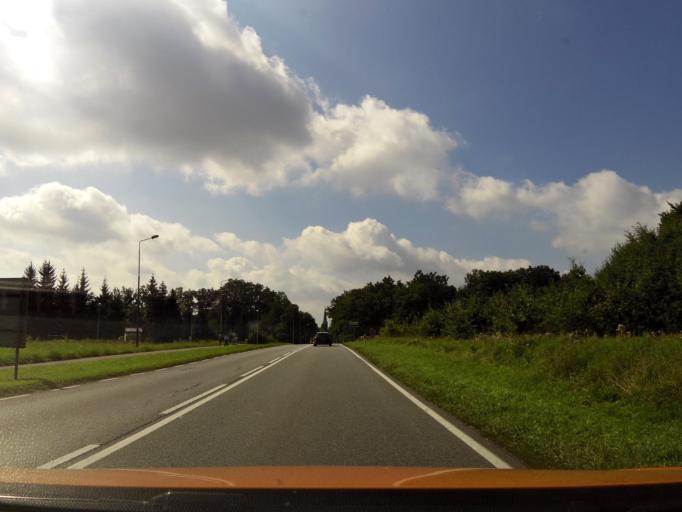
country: PL
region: West Pomeranian Voivodeship
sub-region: Powiat gryficki
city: Ploty
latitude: 53.8094
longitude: 15.2741
